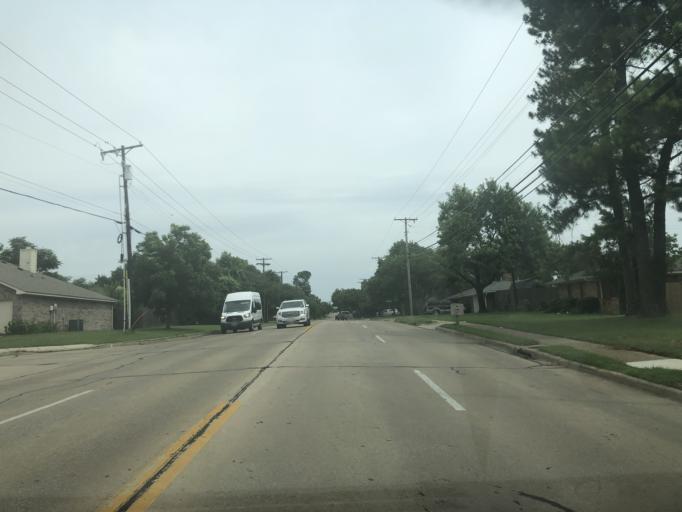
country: US
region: Texas
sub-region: Dallas County
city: Irving
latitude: 32.7949
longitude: -96.9771
